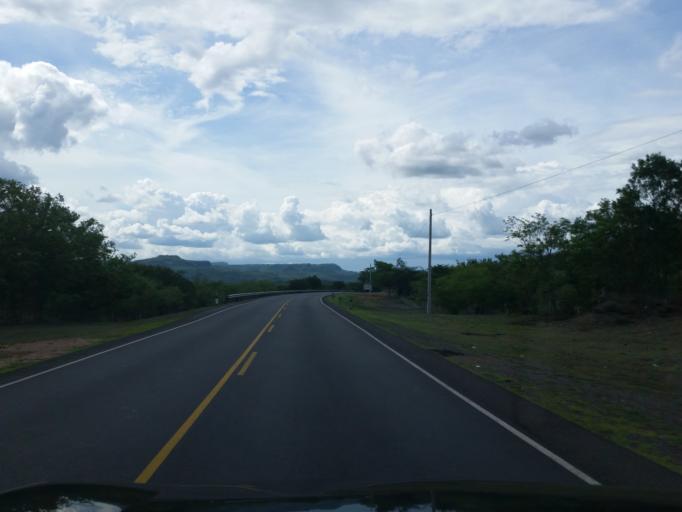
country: NI
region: Matagalpa
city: Ciudad Dario
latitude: 12.6347
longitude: -86.0592
